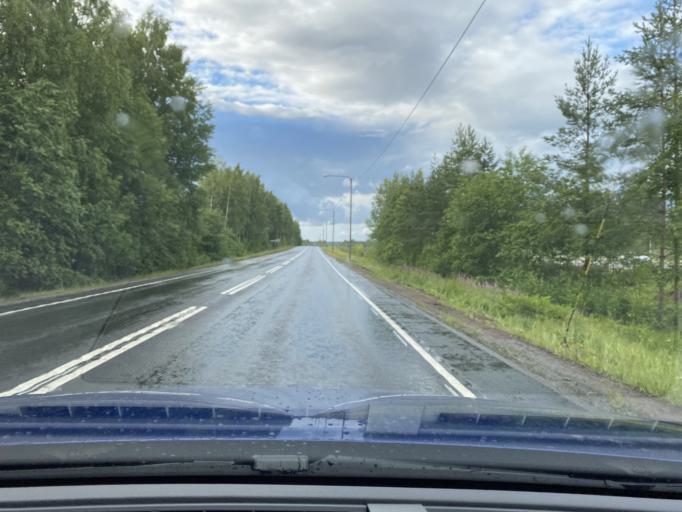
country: FI
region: Uusimaa
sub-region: Helsinki
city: Nurmijaervi
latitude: 60.5043
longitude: 24.8492
